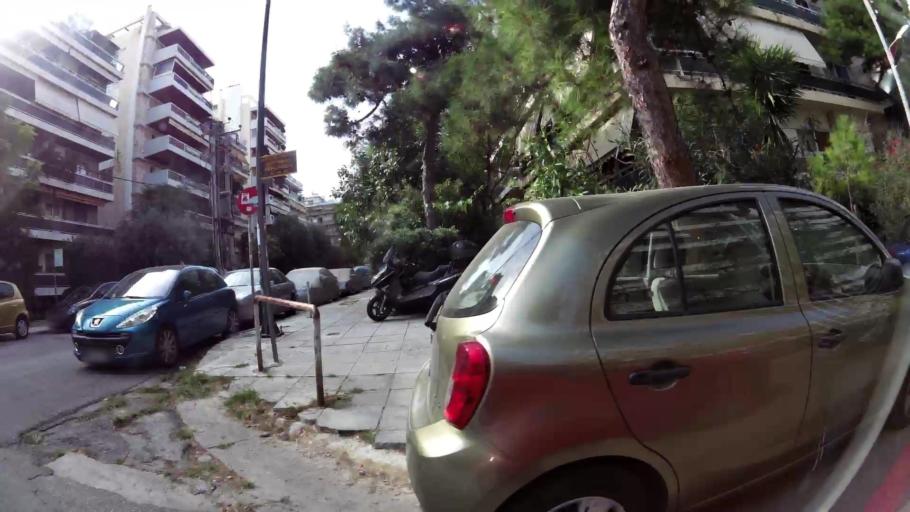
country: GR
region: Attica
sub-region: Nomarchia Athinas
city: Nea Smyrni
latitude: 37.9511
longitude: 23.7149
